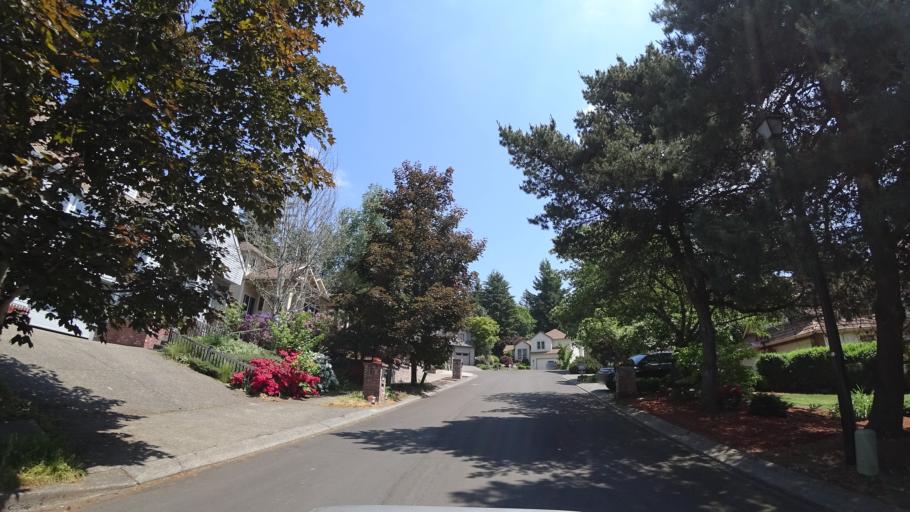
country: US
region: Oregon
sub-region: Washington County
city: Metzger
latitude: 45.4327
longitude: -122.7268
